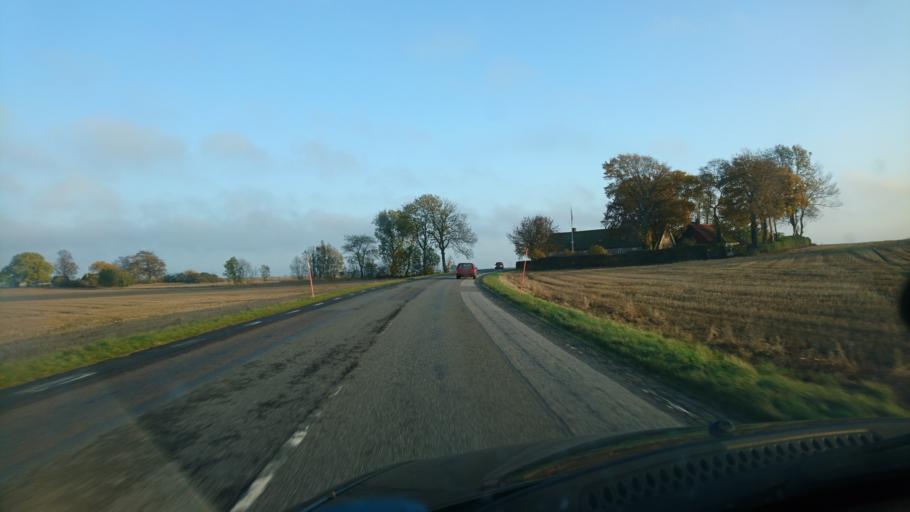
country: SE
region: Skane
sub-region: Tomelilla Kommun
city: Tomelilla
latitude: 55.4594
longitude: 14.1073
